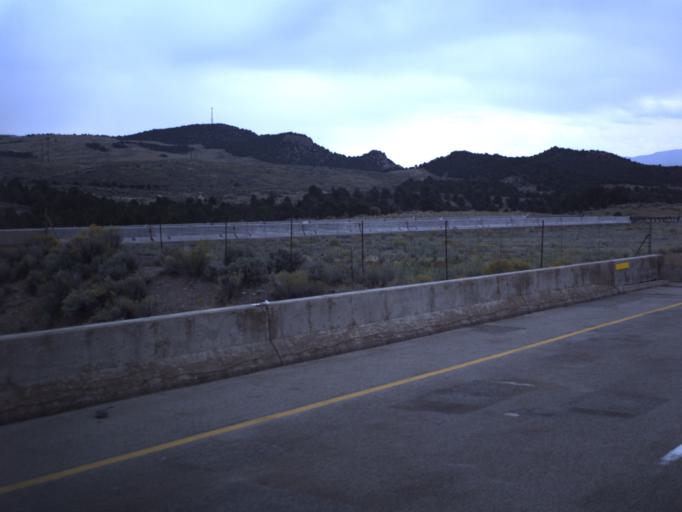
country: US
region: Utah
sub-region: Sevier County
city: Monroe
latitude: 38.5508
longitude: -112.4007
